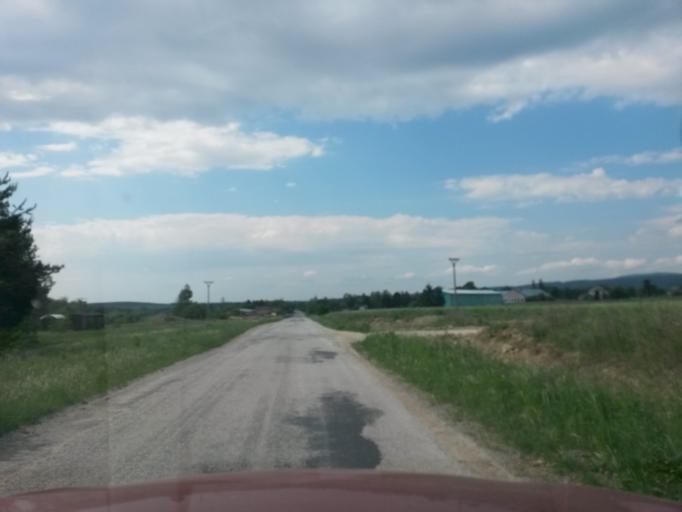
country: SK
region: Kosicky
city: Moldava nad Bodvou
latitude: 48.7001
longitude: 21.0135
